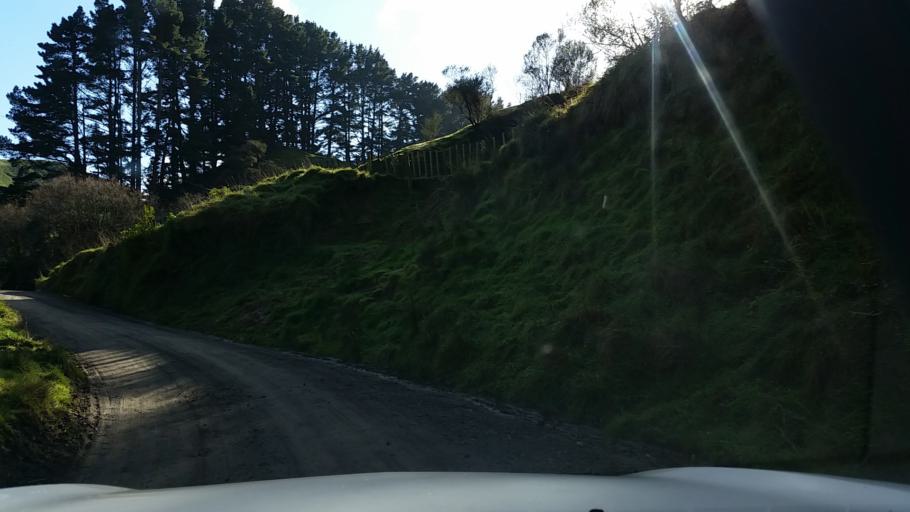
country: NZ
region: Taranaki
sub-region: South Taranaki District
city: Eltham
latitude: -39.5100
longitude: 174.3976
